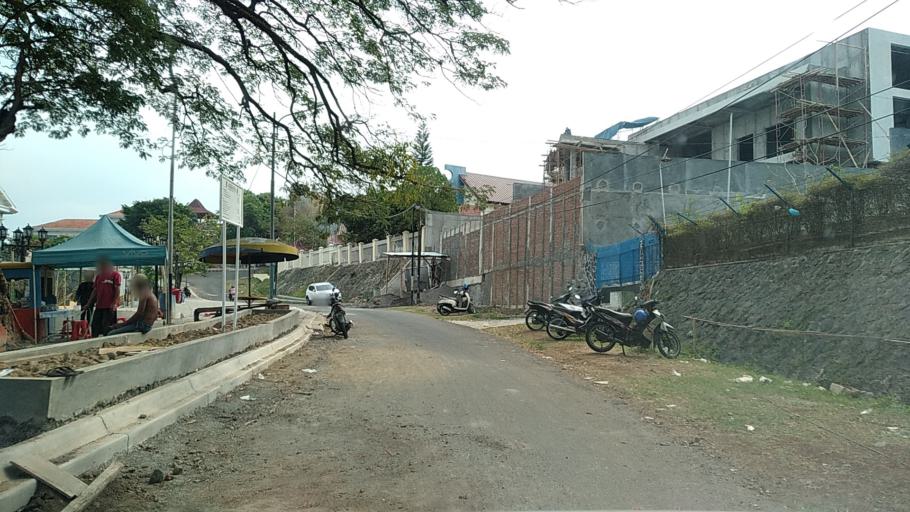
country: ID
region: Central Java
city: Semarang
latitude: -7.0044
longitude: 110.4214
